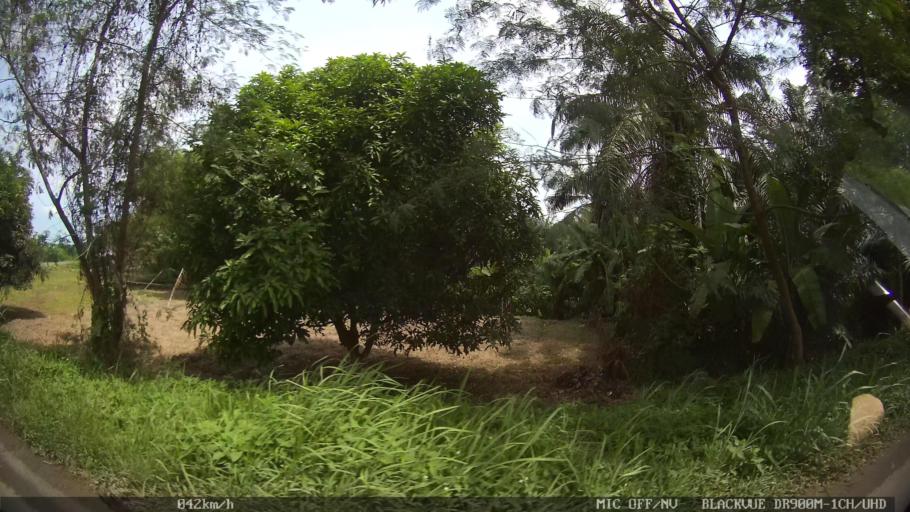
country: ID
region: North Sumatra
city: Percut
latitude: 3.6080
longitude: 98.8429
